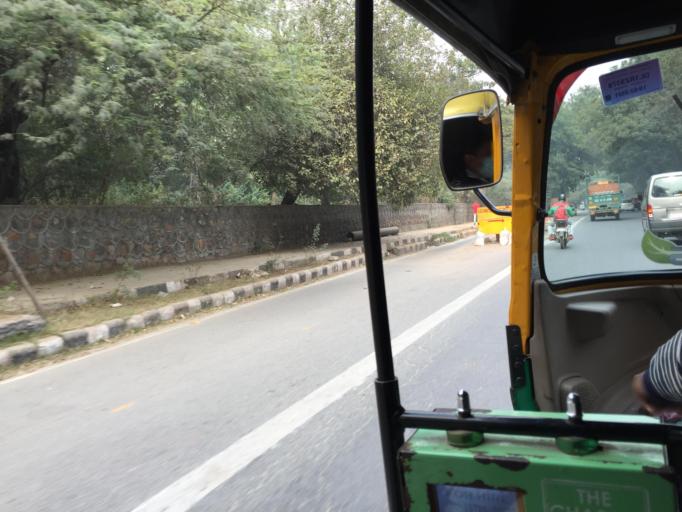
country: IN
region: NCT
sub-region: New Delhi
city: New Delhi
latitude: 28.5163
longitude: 77.1883
